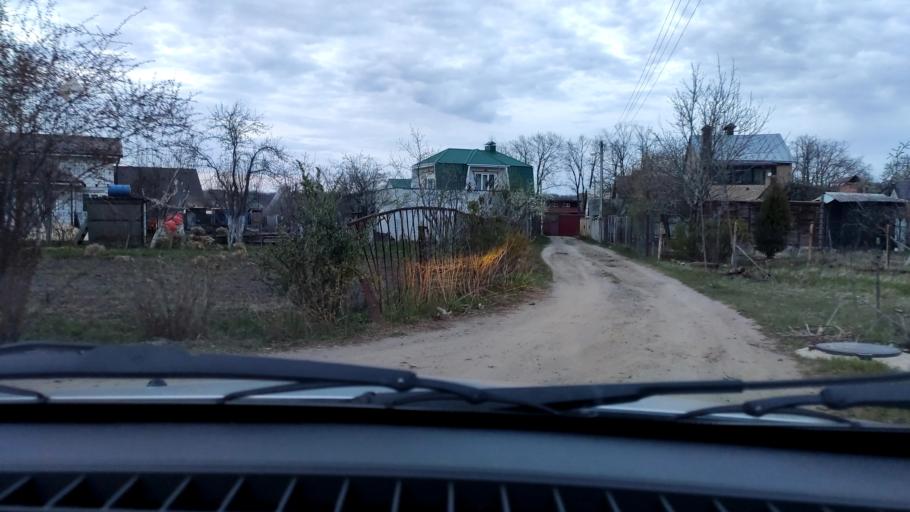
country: RU
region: Voronezj
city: Podgornoye
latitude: 51.7973
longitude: 39.2230
